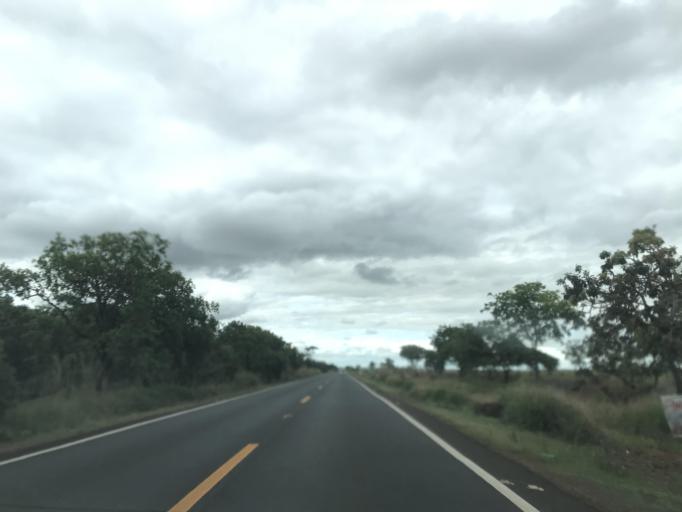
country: BR
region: Goias
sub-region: Caldas Novas
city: Caldas Novas
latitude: -17.5652
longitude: -48.7234
